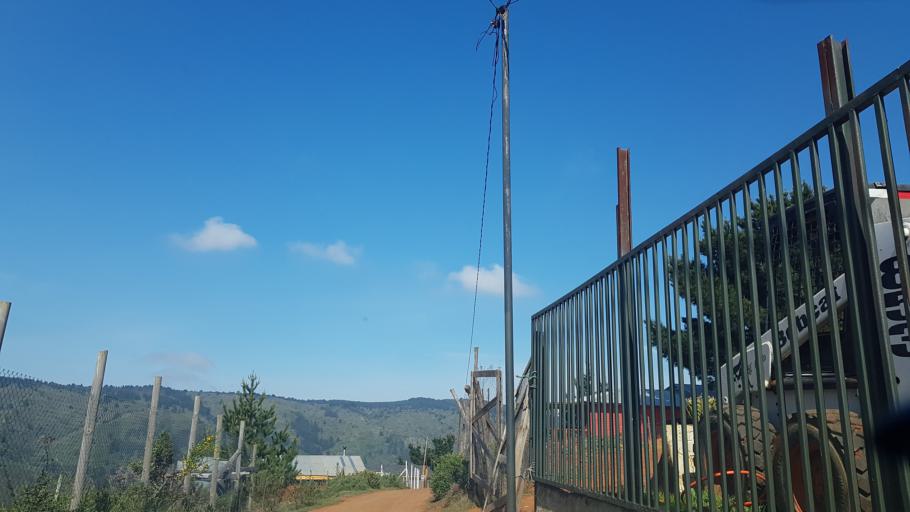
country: CL
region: Valparaiso
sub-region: Provincia de Valparaiso
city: Valparaiso
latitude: -33.1381
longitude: -71.6589
